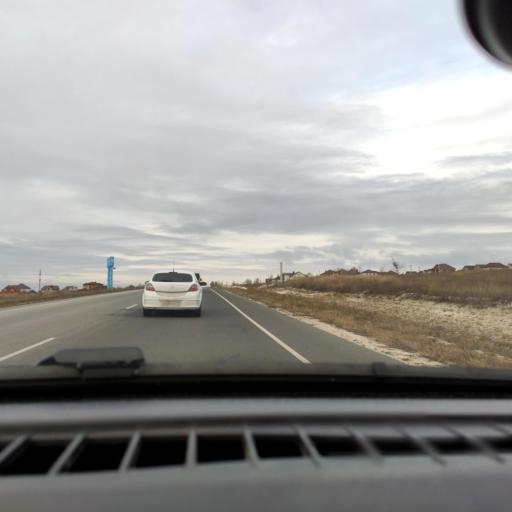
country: RU
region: Belgorod
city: Alekseyevka
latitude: 50.6455
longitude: 38.6379
